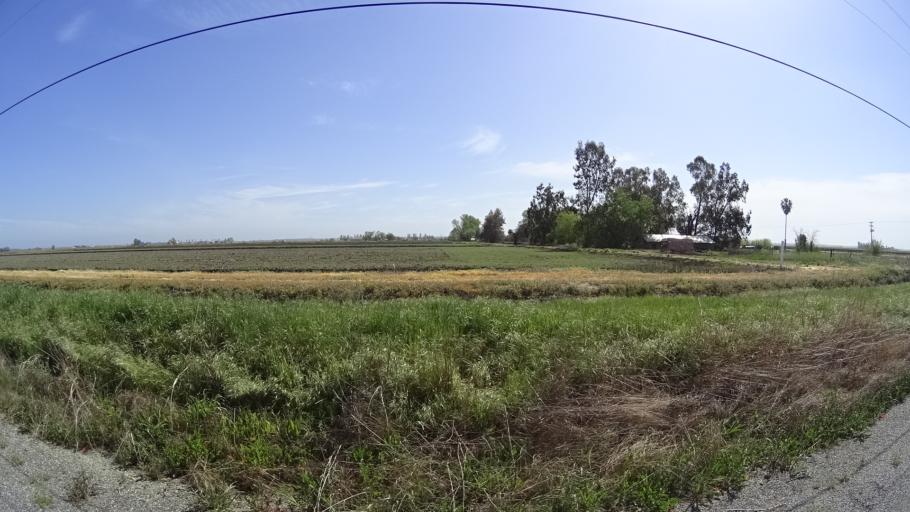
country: US
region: California
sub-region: Glenn County
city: Willows
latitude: 39.5839
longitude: -122.0557
